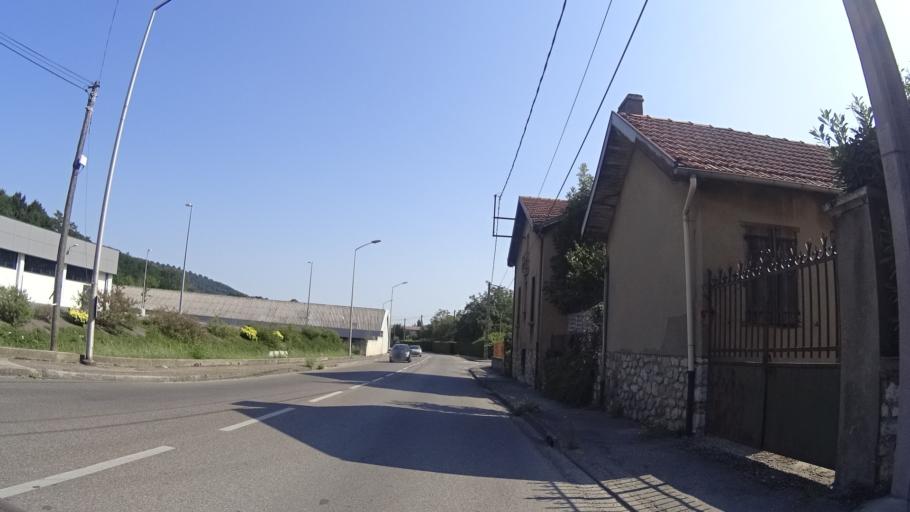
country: FR
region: Midi-Pyrenees
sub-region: Departement de l'Ariege
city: Lavelanet
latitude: 42.9424
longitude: 1.8563
